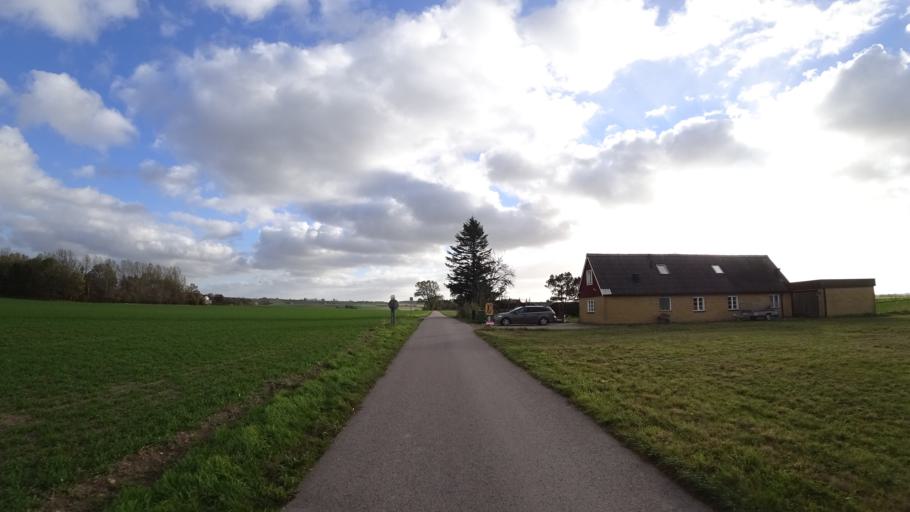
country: SE
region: Skane
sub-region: Staffanstorps Kommun
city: Staffanstorp
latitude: 55.6195
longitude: 13.2047
